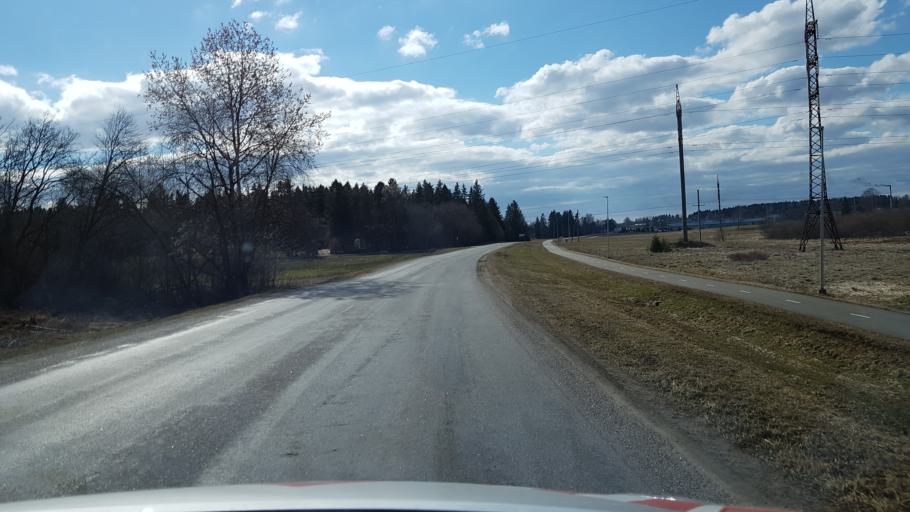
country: EE
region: Laeaene-Virumaa
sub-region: Rakvere linn
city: Rakvere
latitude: 59.3353
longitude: 26.3328
